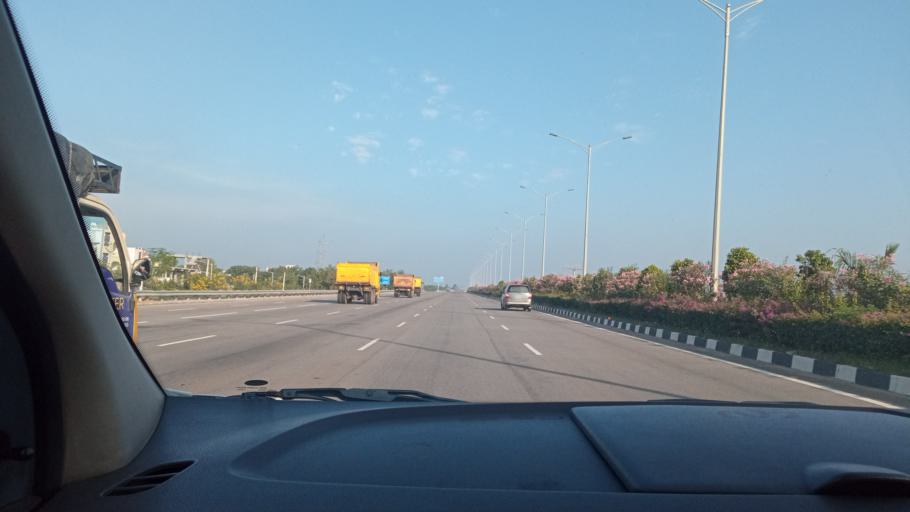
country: IN
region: Telangana
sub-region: Hyderabad
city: Hyderabad
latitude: 17.3423
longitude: 78.3643
